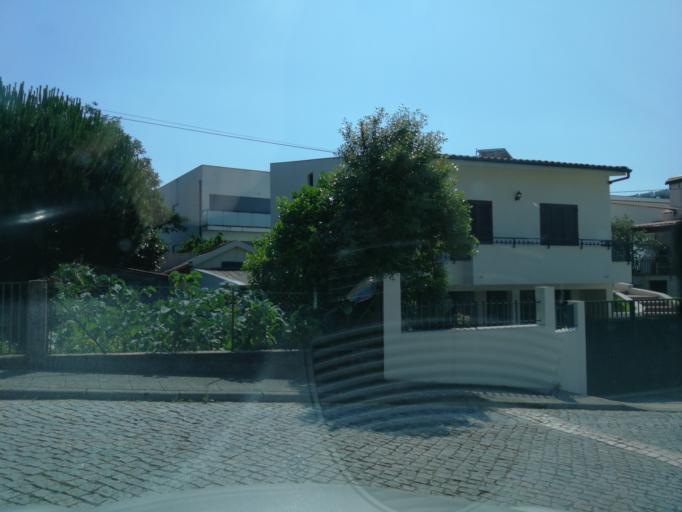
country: PT
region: Braga
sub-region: Braga
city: Adaufe
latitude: 41.5645
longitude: -8.3944
